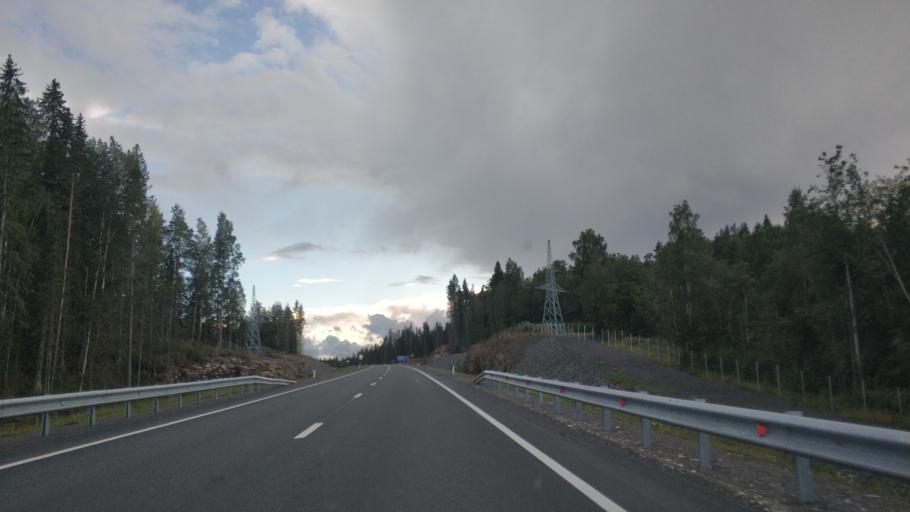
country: RU
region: Republic of Karelia
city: Lakhdenpokh'ya
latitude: 61.4694
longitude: 30.0034
